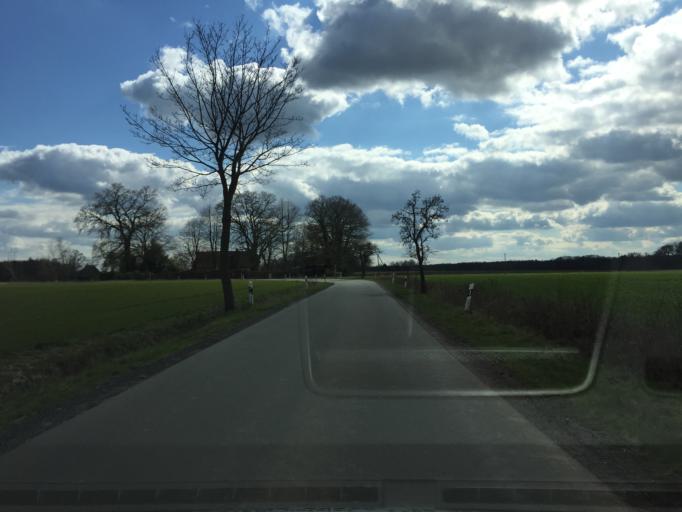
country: DE
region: Lower Saxony
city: Engeln
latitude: 52.7610
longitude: 8.9359
